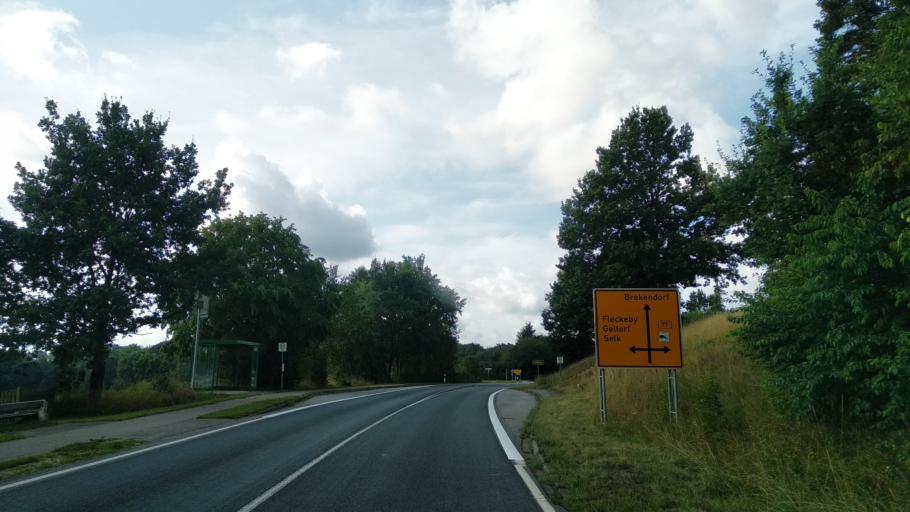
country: DE
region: Schleswig-Holstein
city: Selk
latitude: 54.4779
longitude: 9.5665
